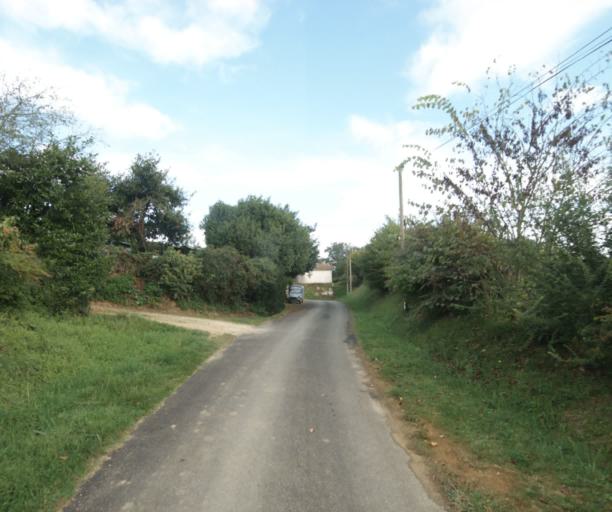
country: FR
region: Midi-Pyrenees
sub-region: Departement du Gers
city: Cazaubon
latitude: 43.8682
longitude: -0.1109
